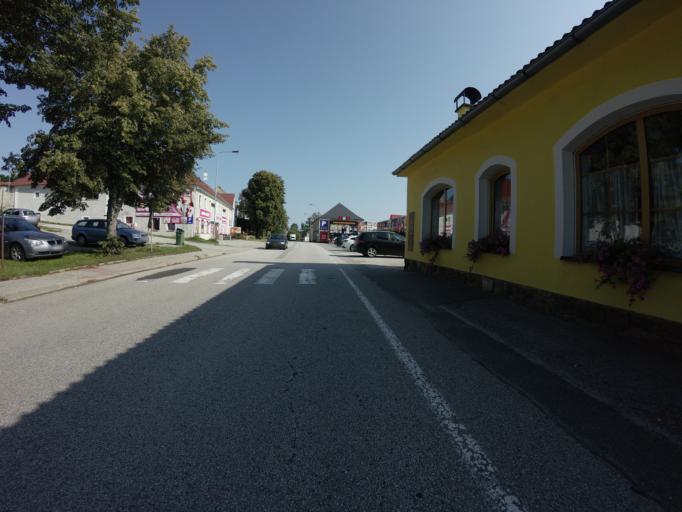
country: CZ
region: Jihocesky
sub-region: Okres Cesky Krumlov
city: Vyssi Brod
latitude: 48.5891
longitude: 14.3259
